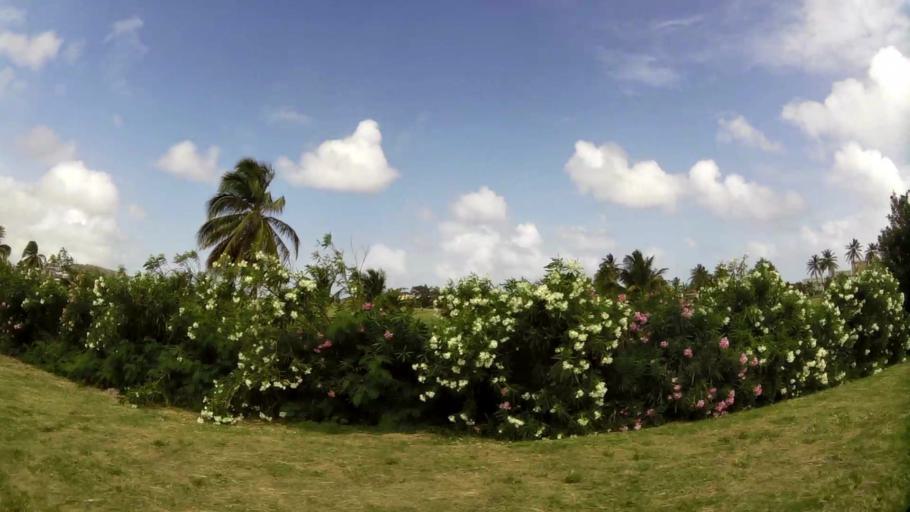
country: KN
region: Saint George Basseterre
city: Basseterre
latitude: 17.2844
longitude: -62.6867
